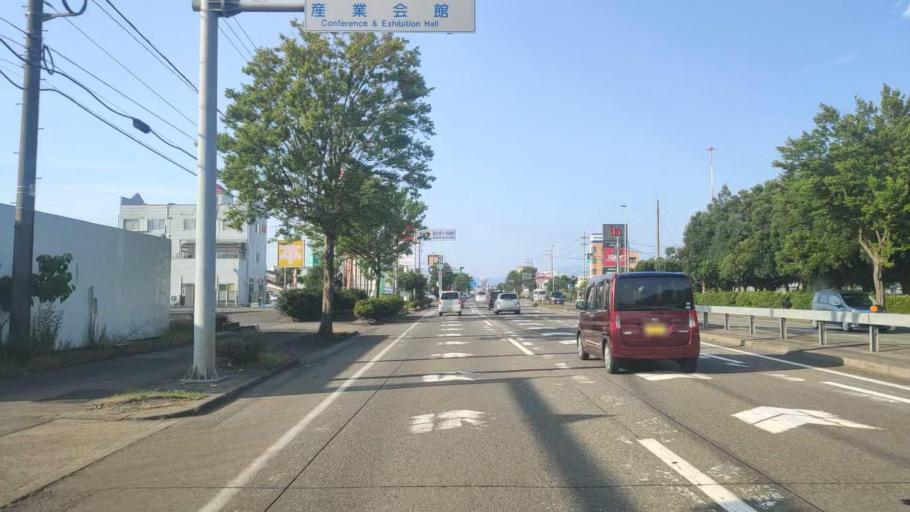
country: JP
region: Fukui
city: Fukui-shi
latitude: 36.0375
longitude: 136.2295
